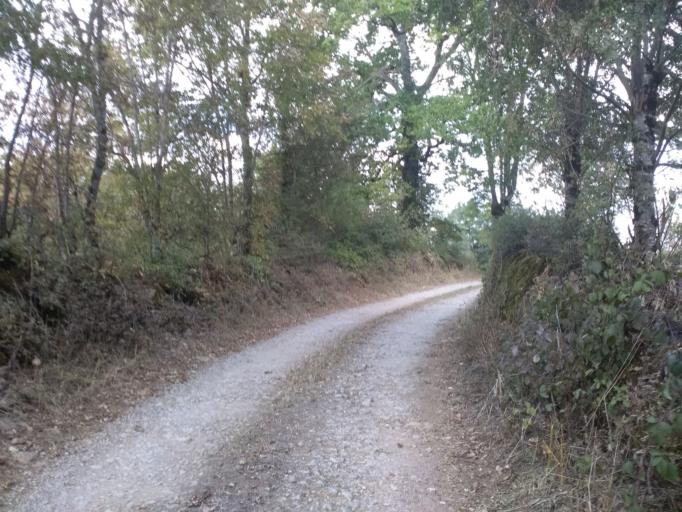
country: FR
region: Midi-Pyrenees
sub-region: Departement de l'Aveyron
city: Bozouls
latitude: 44.4662
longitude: 2.6734
